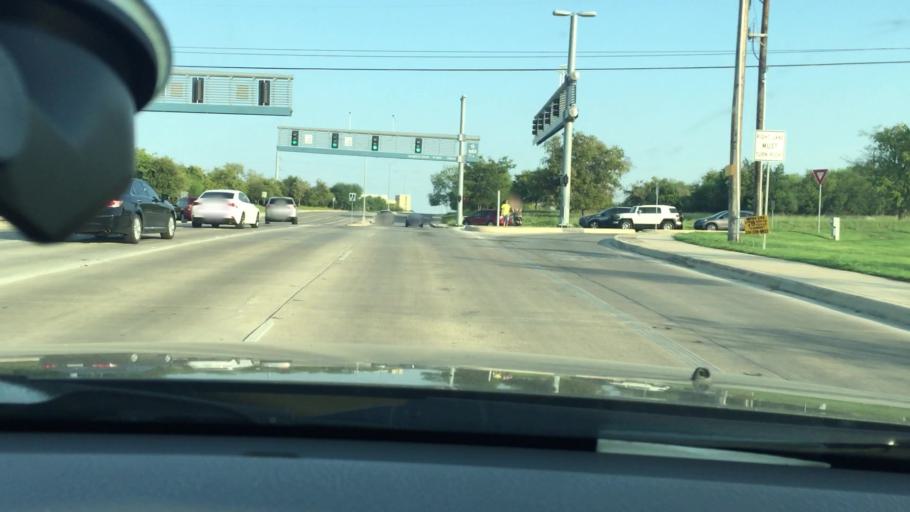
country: US
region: Texas
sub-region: Bexar County
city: Leon Valley
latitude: 29.5205
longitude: -98.5890
